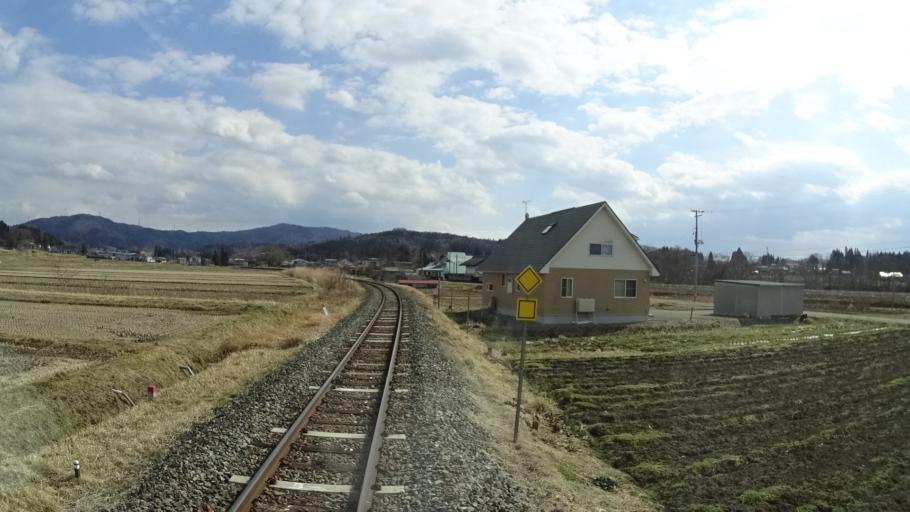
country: JP
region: Iwate
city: Hanamaki
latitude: 39.3690
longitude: 141.2562
